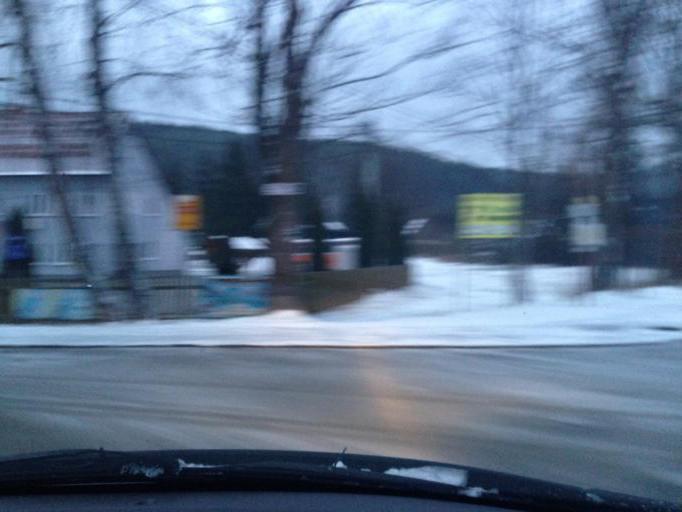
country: PL
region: Subcarpathian Voivodeship
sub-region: Powiat jasielski
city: Krempna
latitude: 49.5113
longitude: 21.5007
